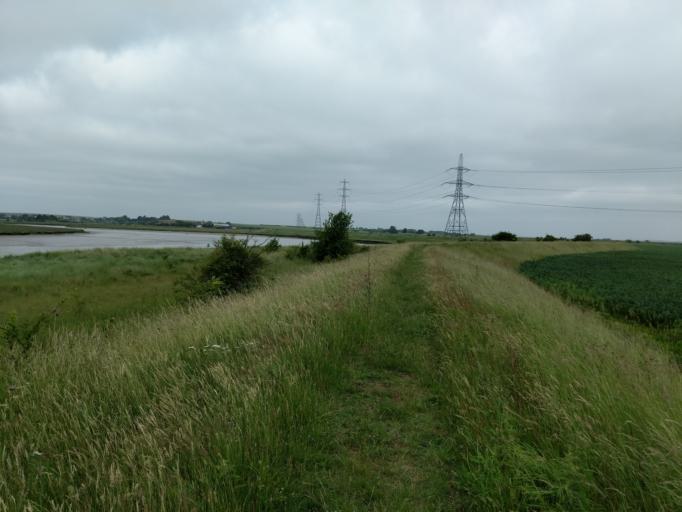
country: GB
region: England
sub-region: Kent
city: Faversham
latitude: 51.3361
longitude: 0.9075
